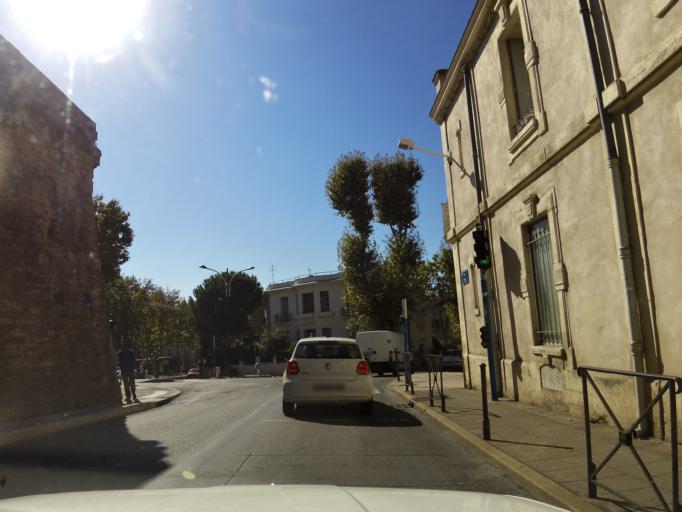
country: FR
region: Languedoc-Roussillon
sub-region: Departement de l'Herault
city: Montpellier
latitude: 43.6123
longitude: 3.8685
